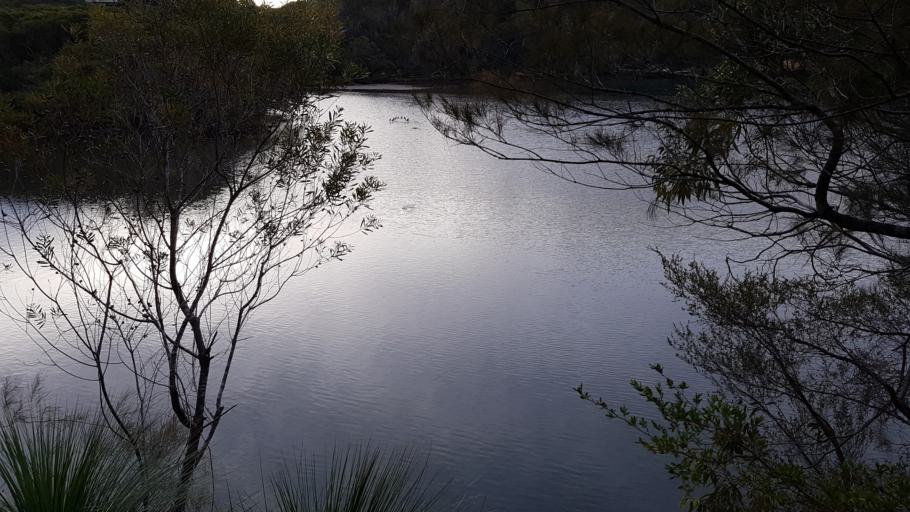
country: AU
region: New South Wales
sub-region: Willoughby
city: Castlecrag
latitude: -33.7926
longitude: 151.2187
